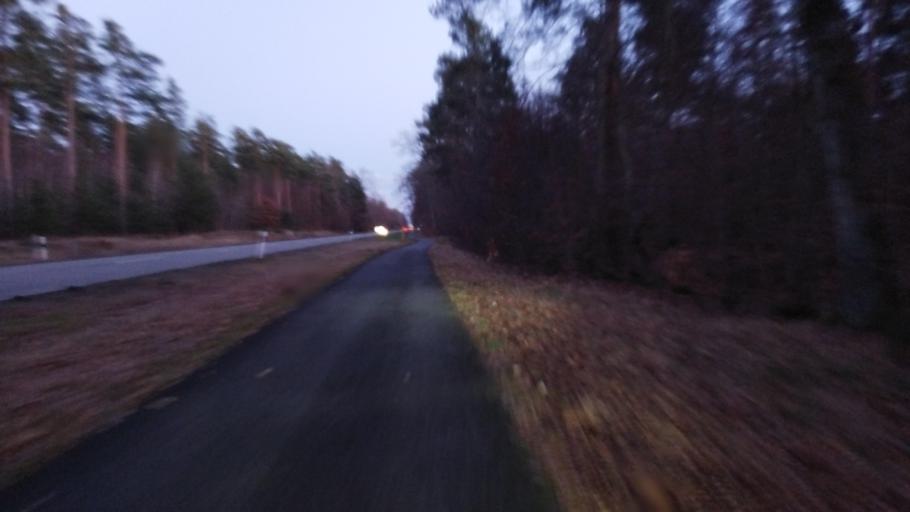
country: DE
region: Rheinland-Pfalz
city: Dudenhofen
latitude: 49.3433
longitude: 8.3894
